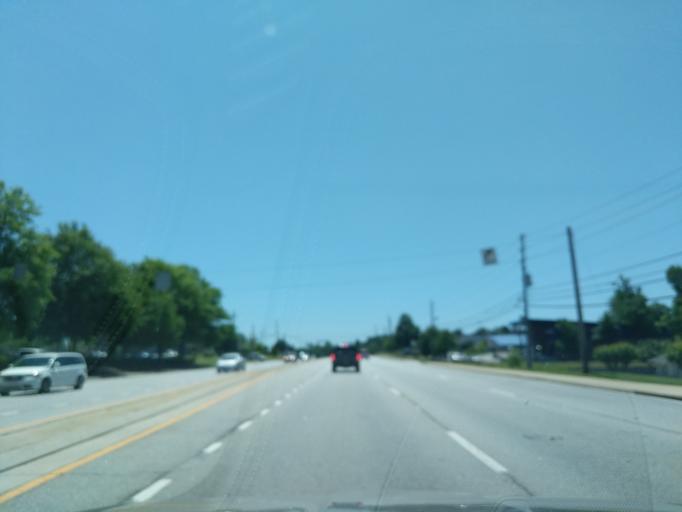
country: US
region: Georgia
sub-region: Columbia County
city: Martinez
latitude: 33.5298
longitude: -82.0747
